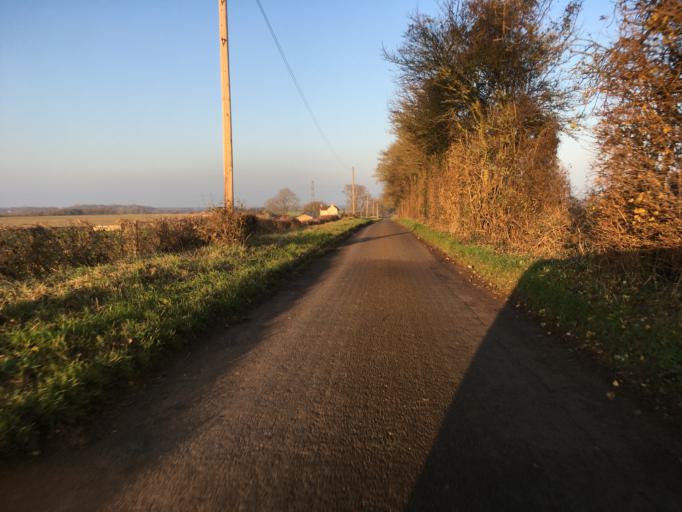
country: GB
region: England
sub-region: Wiltshire
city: Nettleton
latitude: 51.4768
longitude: -2.2702
